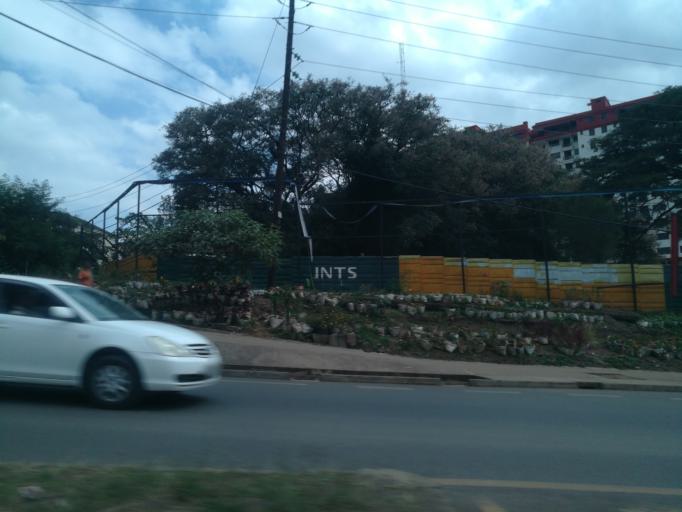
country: KE
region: Nairobi Area
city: Nairobi
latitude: -1.2849
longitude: 36.7879
